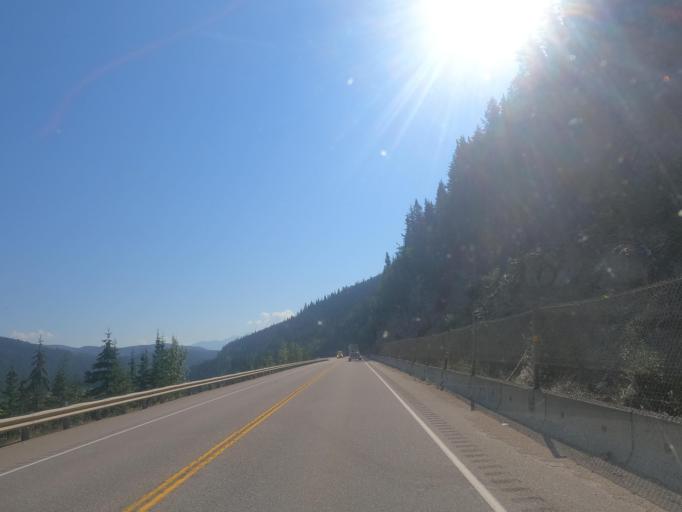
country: CA
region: Alberta
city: Jasper Park Lodge
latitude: 52.8735
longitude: -118.3053
